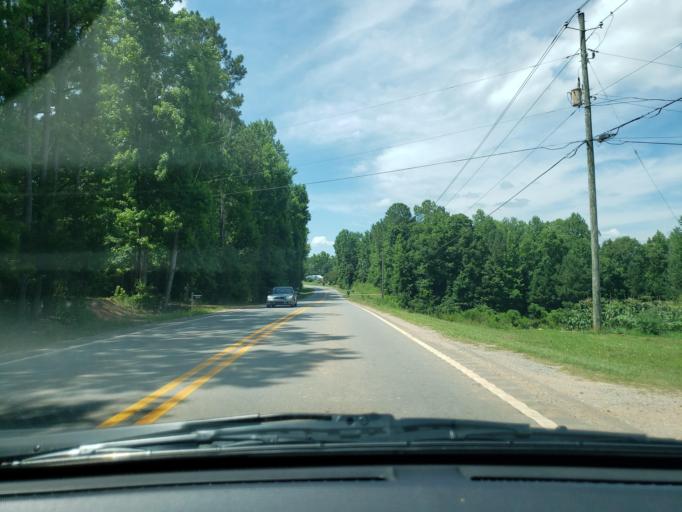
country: US
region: Alabama
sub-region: Elmore County
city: Eclectic
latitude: 32.6668
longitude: -85.9423
